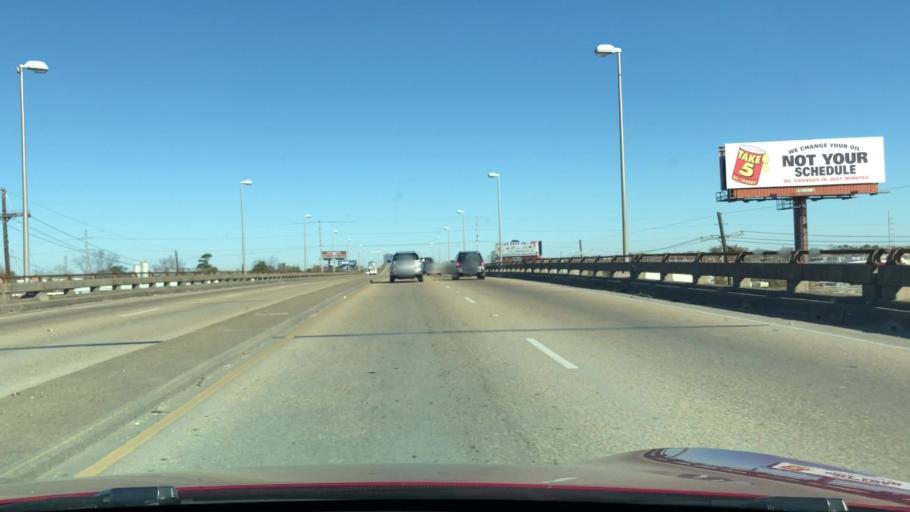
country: US
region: Louisiana
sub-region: Jefferson Parish
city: Jefferson
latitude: 29.9697
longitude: -90.1566
